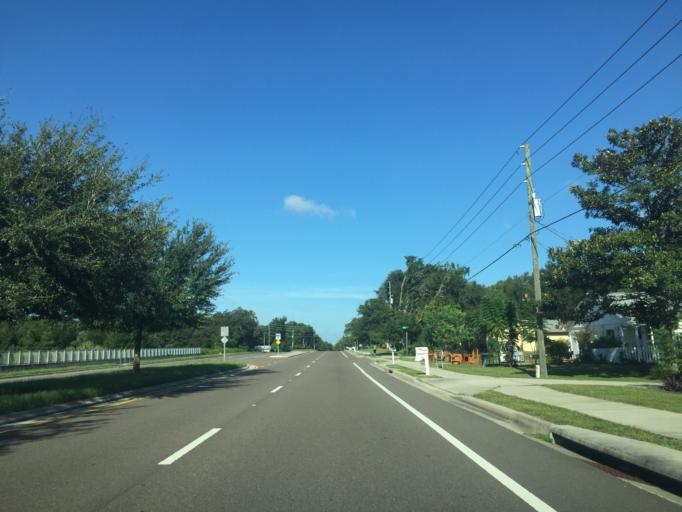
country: US
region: Florida
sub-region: Seminole County
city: Winter Springs
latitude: 28.6705
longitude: -81.2945
